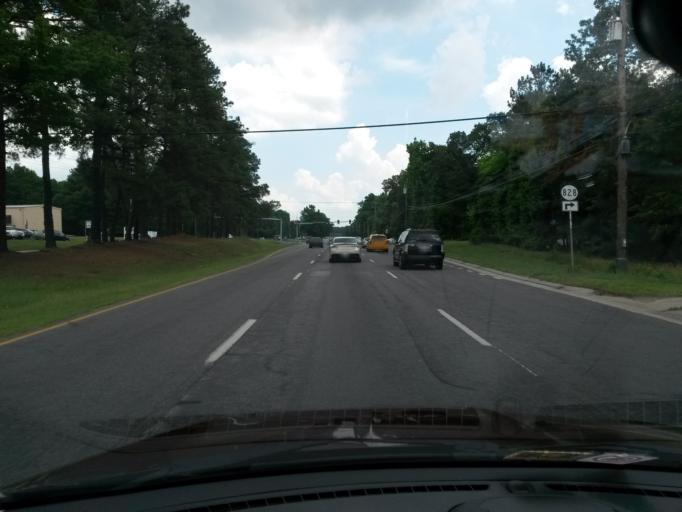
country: US
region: Virginia
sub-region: Chesterfield County
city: Enon
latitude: 37.3476
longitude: -77.3519
